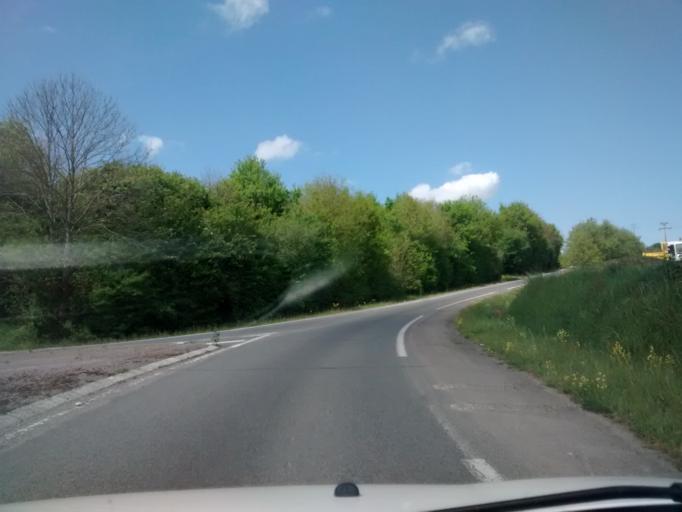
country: FR
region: Brittany
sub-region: Departement des Cotes-d'Armor
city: Saint-Samson-sur-Rance
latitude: 48.4814
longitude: -2.0424
